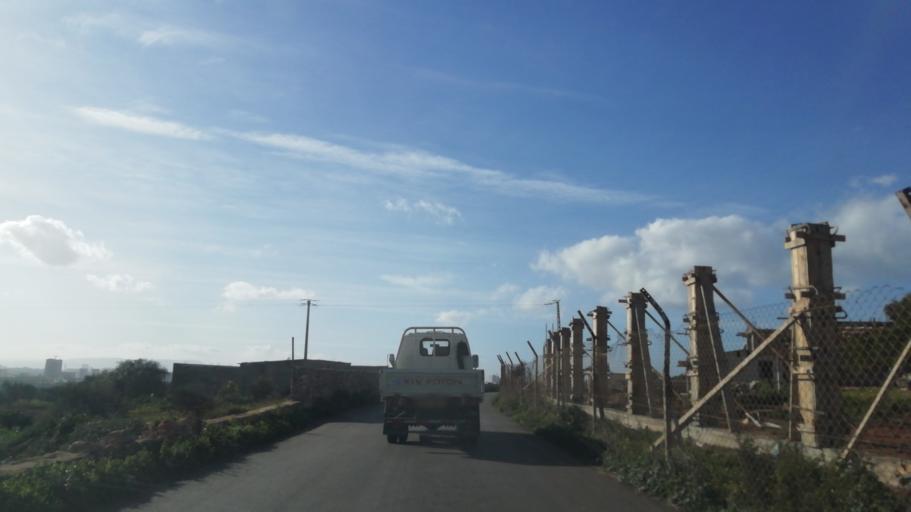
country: DZ
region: Oran
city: Bir el Djir
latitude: 35.7521
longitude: -0.5121
